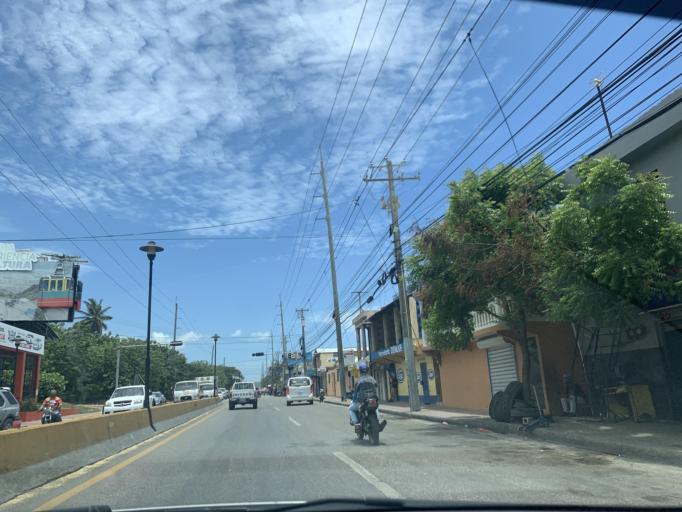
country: DO
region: Puerto Plata
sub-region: Puerto Plata
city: Puerto Plata
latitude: 19.7928
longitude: -70.7082
